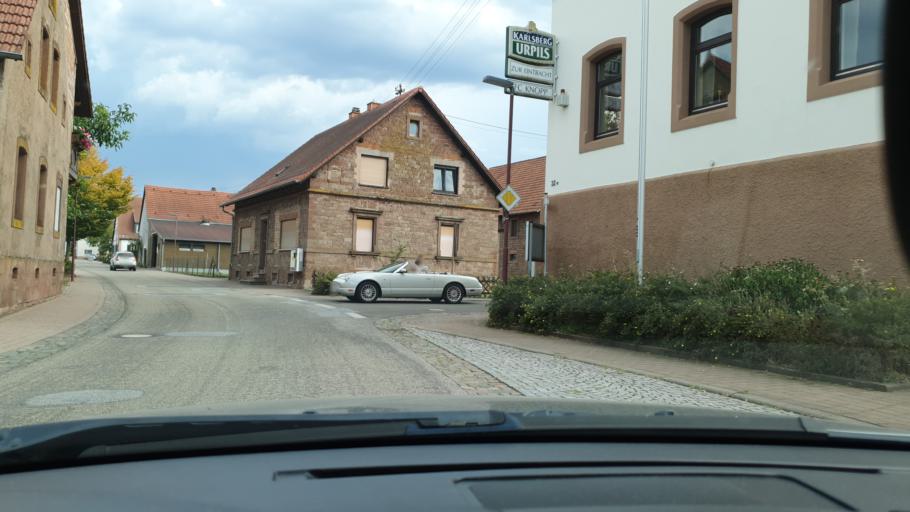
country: DE
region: Rheinland-Pfalz
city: Knopp-Labach
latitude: 49.3327
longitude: 7.5081
